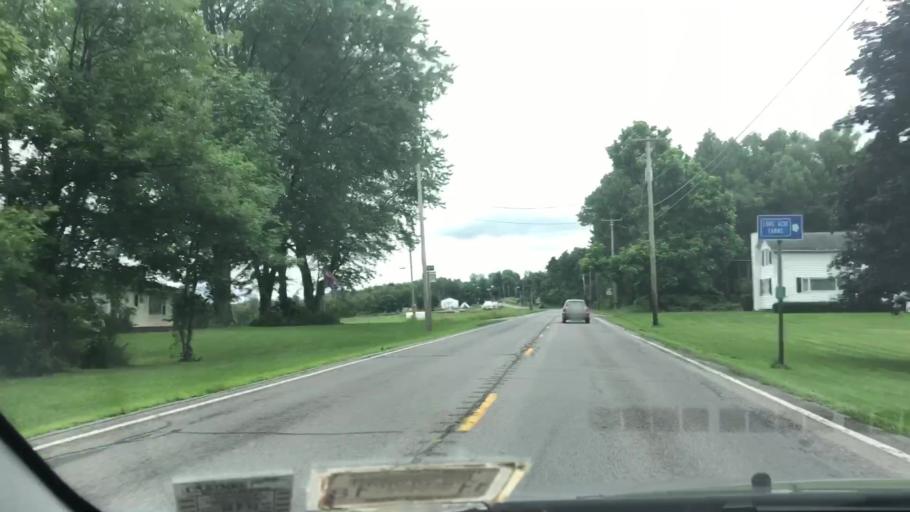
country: US
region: New York
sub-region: Wayne County
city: Macedon
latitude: 43.1187
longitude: -77.2932
